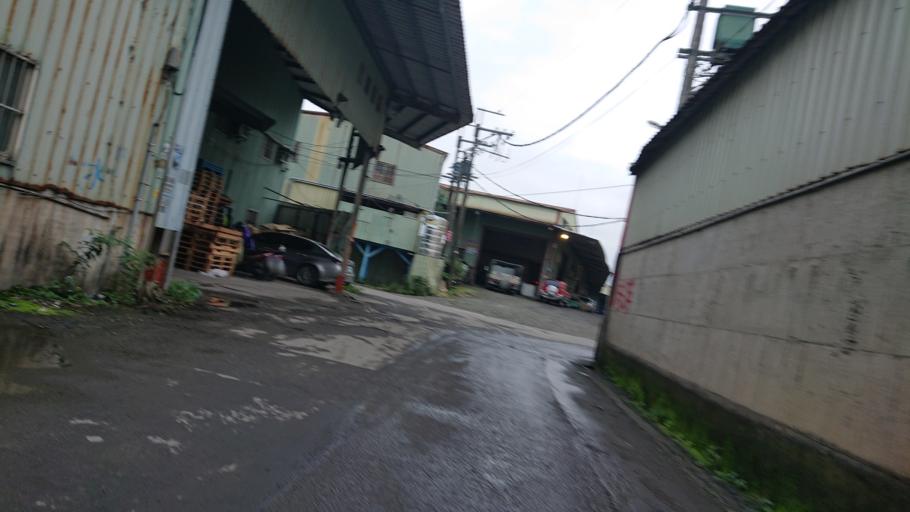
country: TW
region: Taiwan
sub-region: Taoyuan
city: Taoyuan
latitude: 24.9444
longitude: 121.3956
